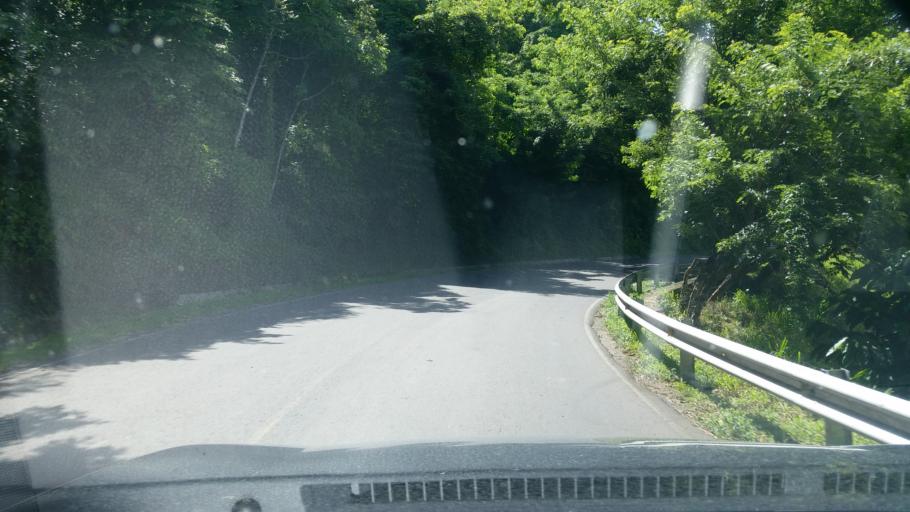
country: NI
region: Matagalpa
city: San Ramon
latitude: 13.0152
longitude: -85.7895
